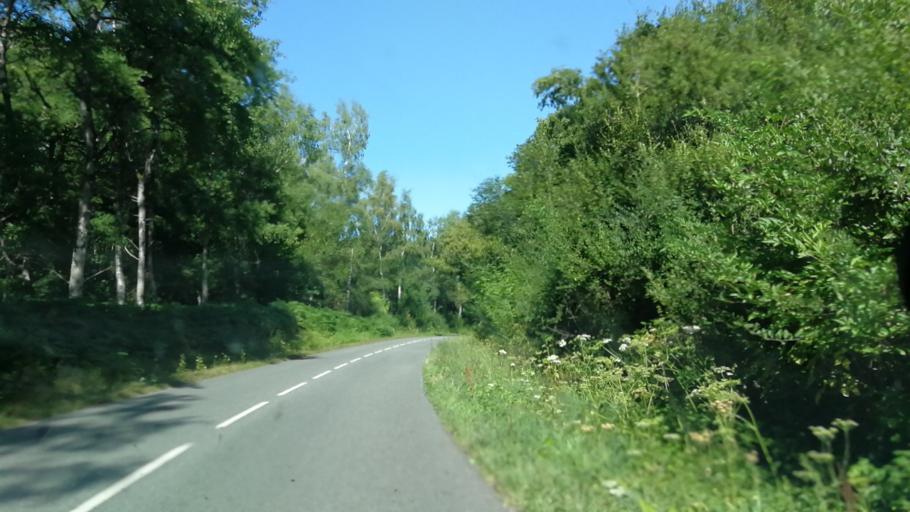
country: FR
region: Ile-de-France
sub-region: Departement des Yvelines
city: Cernay-la-Ville
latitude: 48.6786
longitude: 1.9470
